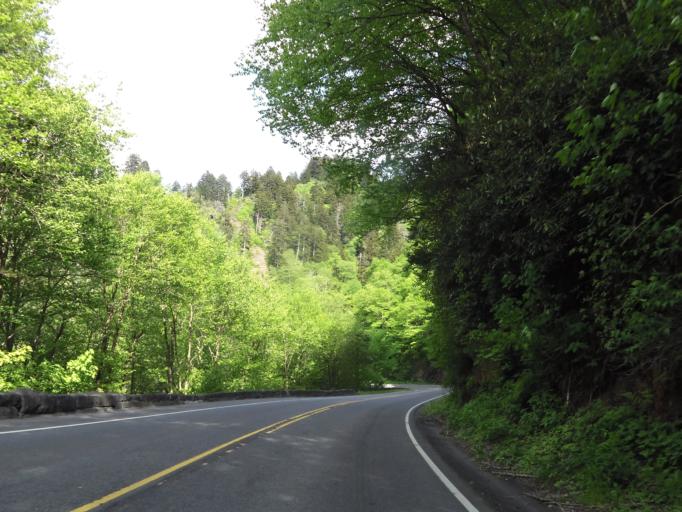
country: US
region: Tennessee
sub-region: Sevier County
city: Gatlinburg
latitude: 35.6243
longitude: -83.4186
